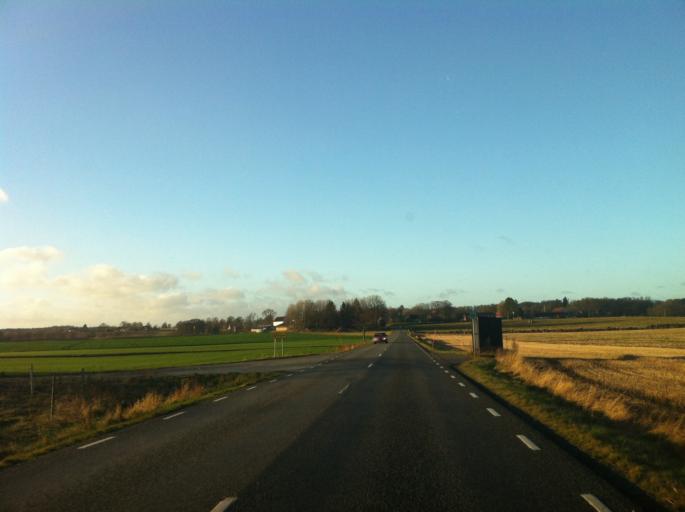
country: SE
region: Skane
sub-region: Ostra Goinge Kommun
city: Knislinge
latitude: 56.1863
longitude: 14.0059
